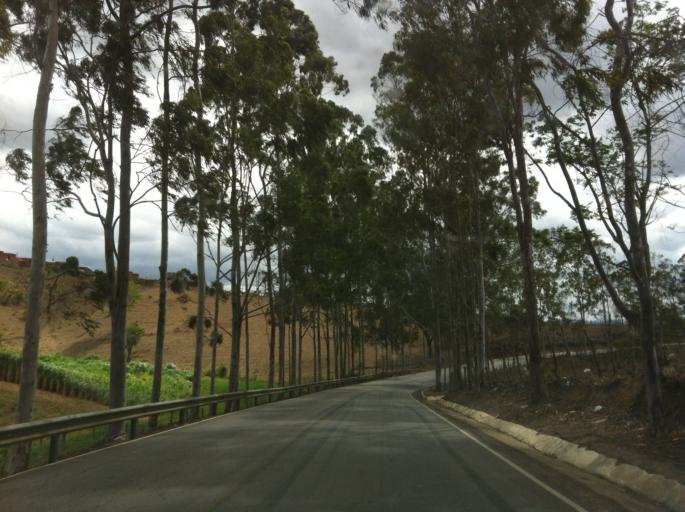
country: BR
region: Alagoas
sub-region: Ibateguara
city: Ibateguara
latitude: -8.9661
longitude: -35.9271
